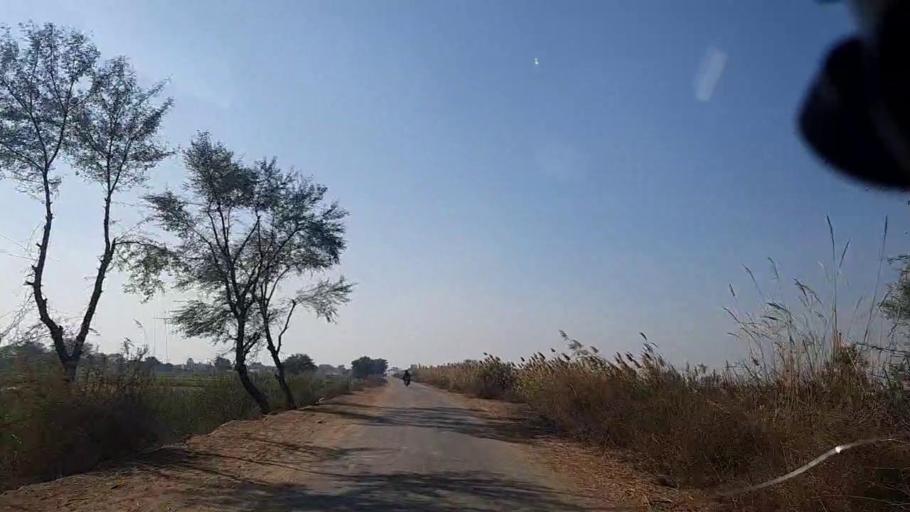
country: PK
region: Sindh
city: Khanpur
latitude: 27.7299
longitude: 69.4468
